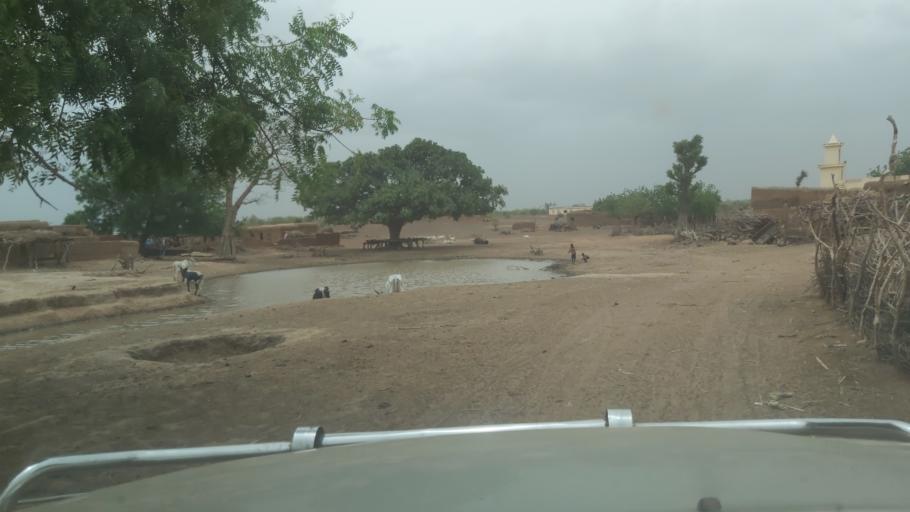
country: ML
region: Koulikoro
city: Banamba
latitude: 13.3761
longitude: -7.2230
